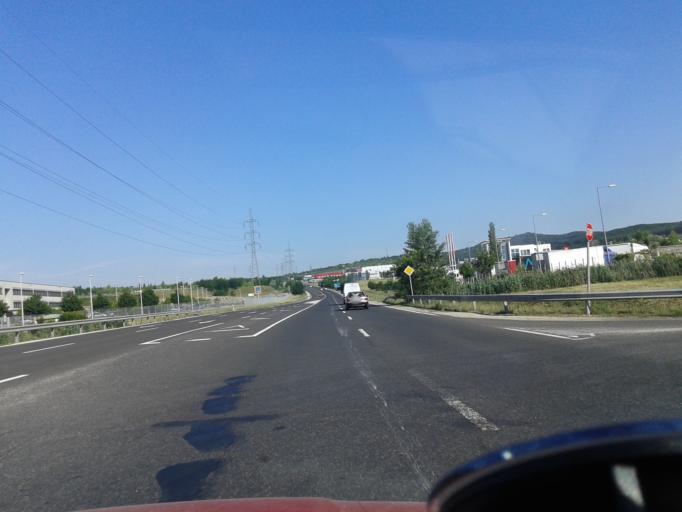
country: HU
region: Pest
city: Biatorbagy
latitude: 47.4690
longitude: 18.8728
